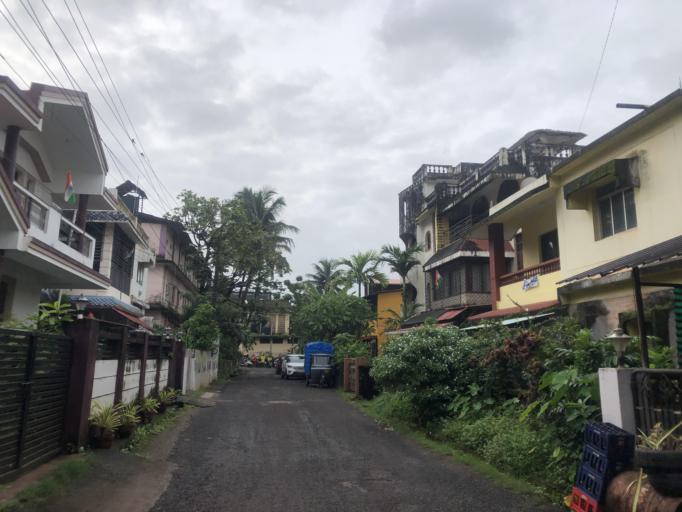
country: IN
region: Goa
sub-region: North Goa
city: Mapuca
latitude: 15.5954
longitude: 73.8042
